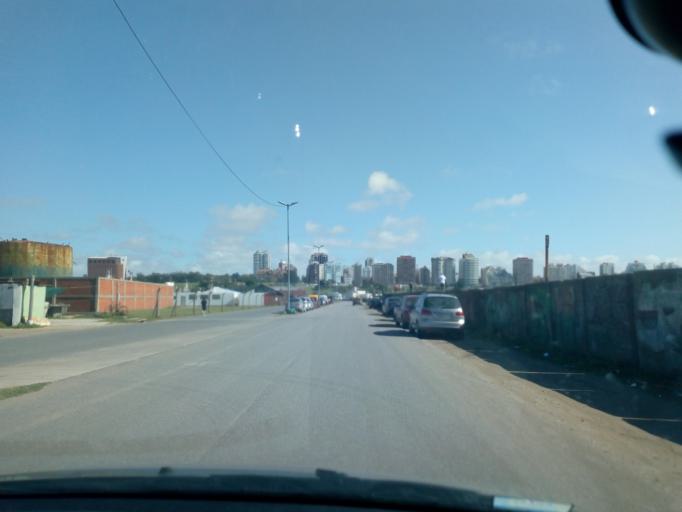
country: AR
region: Buenos Aires
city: Mar del Plata
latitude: -38.0344
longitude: -57.5271
